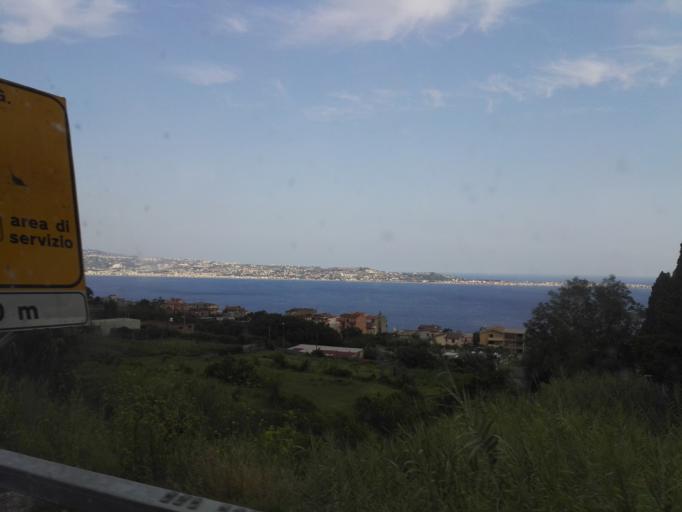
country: IT
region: Calabria
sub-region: Provincia di Reggio Calabria
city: Villa San Giovanni
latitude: 38.2286
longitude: 15.6522
